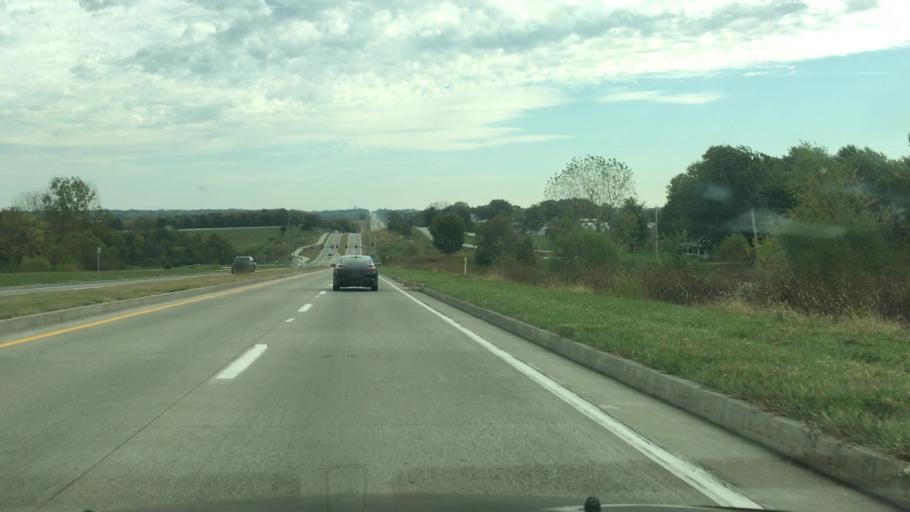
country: US
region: Missouri
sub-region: Jackson County
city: Grandview
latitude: 38.8565
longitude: -94.4857
